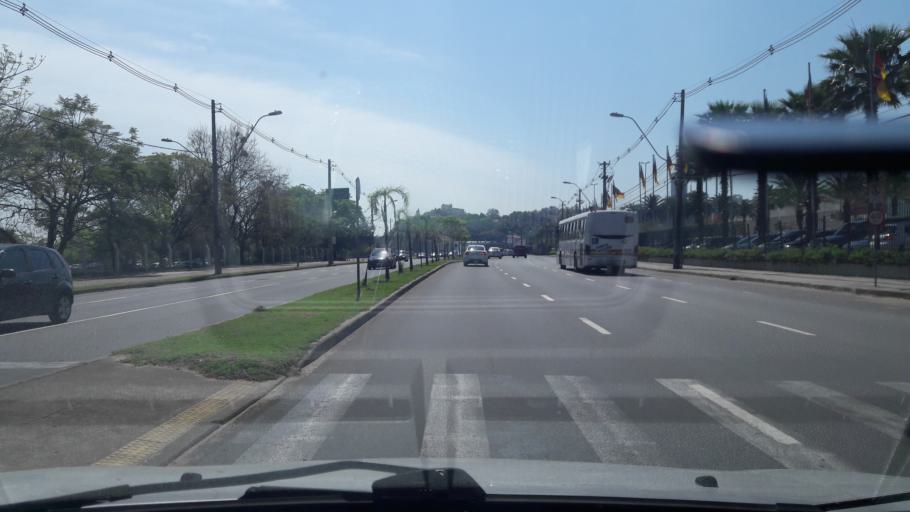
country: BR
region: Rio Grande do Sul
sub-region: Porto Alegre
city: Porto Alegre
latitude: -30.0846
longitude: -51.2473
